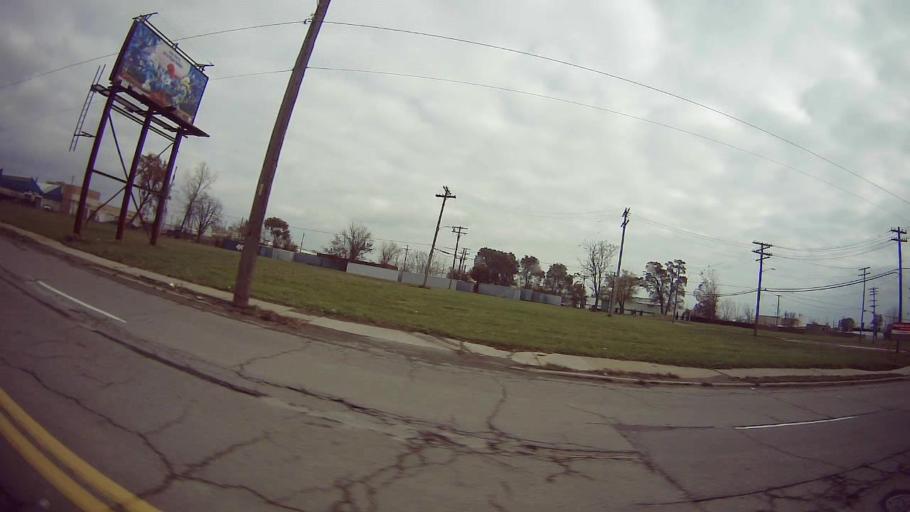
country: US
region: Michigan
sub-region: Wayne County
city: Hamtramck
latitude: 42.3962
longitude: -83.0376
